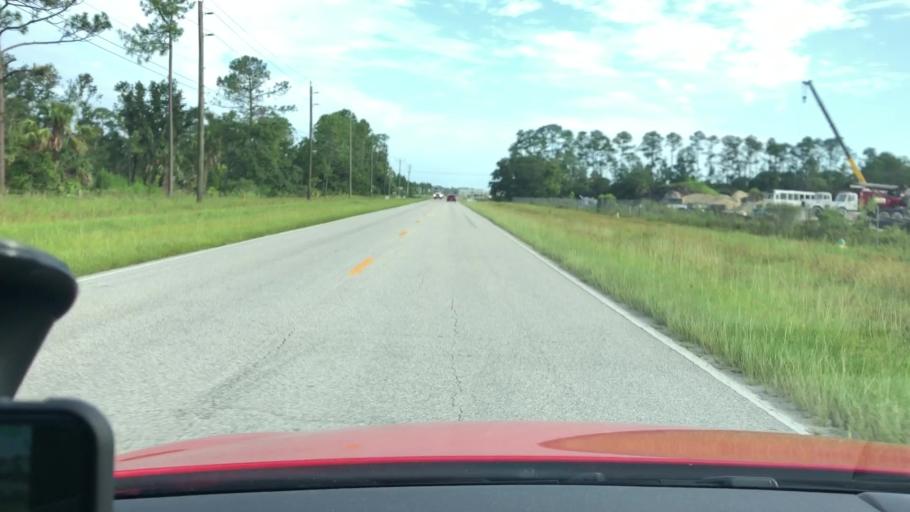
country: US
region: Florida
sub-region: Volusia County
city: Daytona Beach
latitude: 29.1816
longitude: -81.0922
